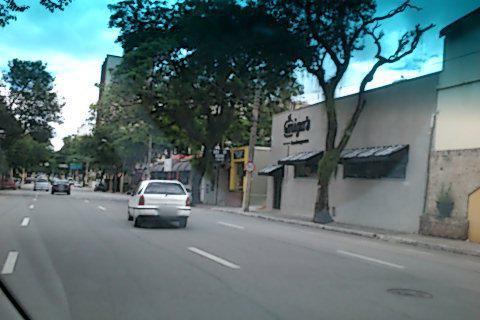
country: BR
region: Sao Paulo
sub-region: Sao Jose Dos Campos
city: Sao Jose dos Campos
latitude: -23.2035
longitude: -45.8969
